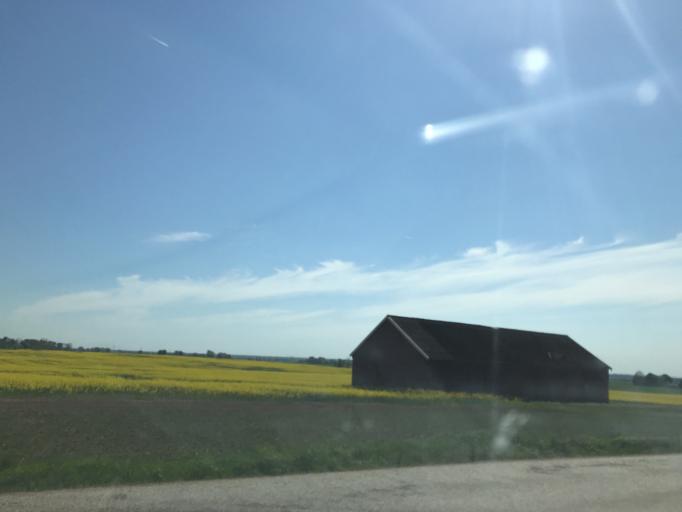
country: SE
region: Skane
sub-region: Svalovs Kommun
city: Teckomatorp
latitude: 55.8989
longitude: 13.0193
